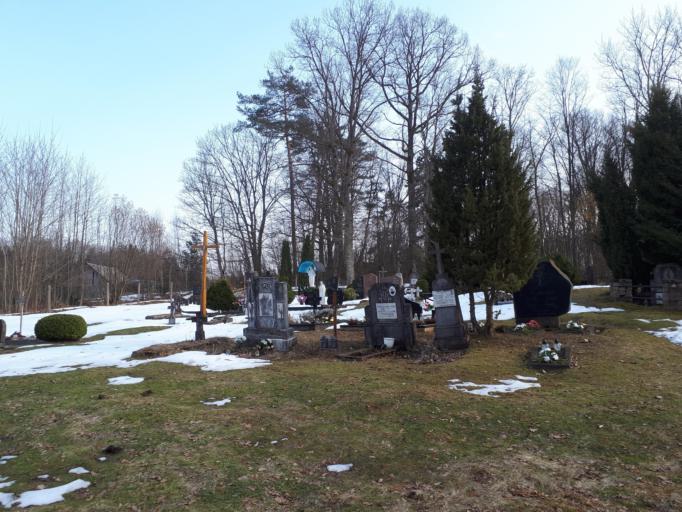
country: LT
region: Alytaus apskritis
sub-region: Alytaus rajonas
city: Daugai
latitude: 54.3997
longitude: 24.2275
